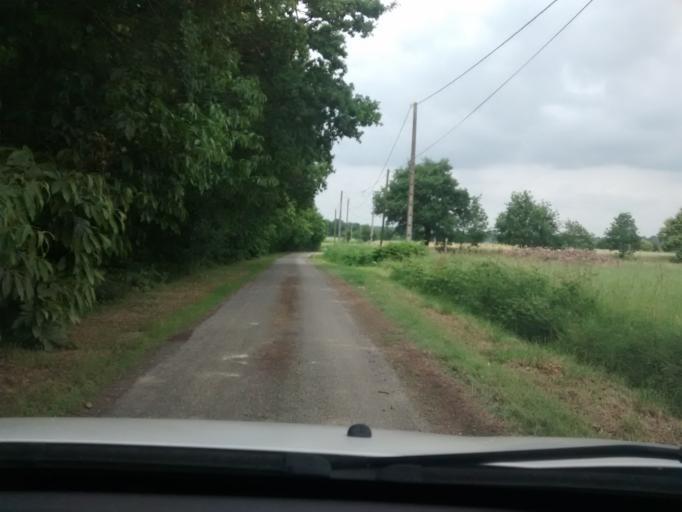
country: FR
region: Brittany
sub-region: Departement d'Ille-et-Vilaine
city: Servon-sur-Vilaine
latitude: 48.1416
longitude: -1.4663
